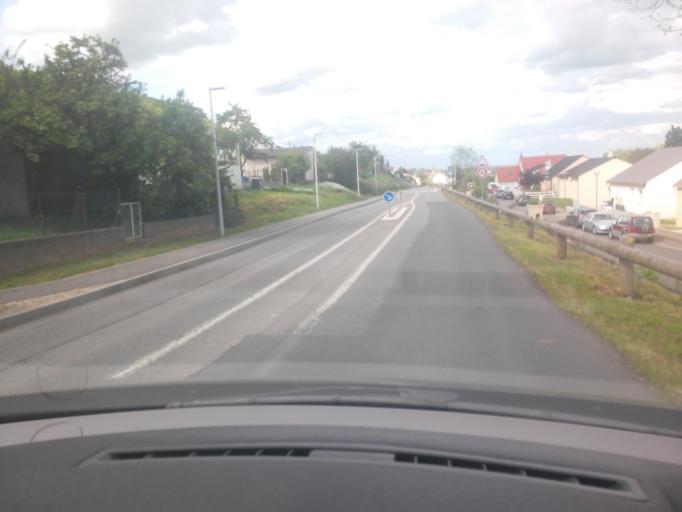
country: FR
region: Lorraine
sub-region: Departement de la Moselle
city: Marange-Silvange
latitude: 49.1930
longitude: 6.0823
